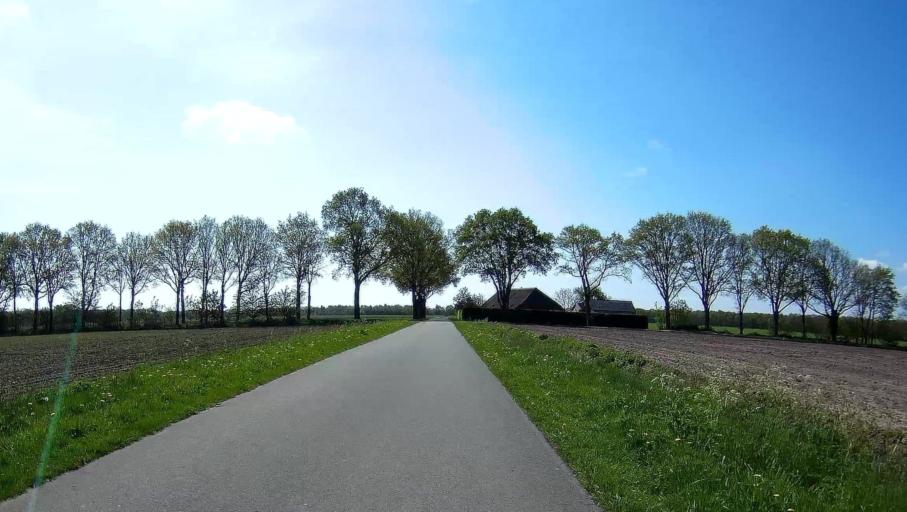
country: NL
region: Drenthe
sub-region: Gemeente Borger-Odoorn
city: Borger
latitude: 52.9886
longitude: 6.7907
